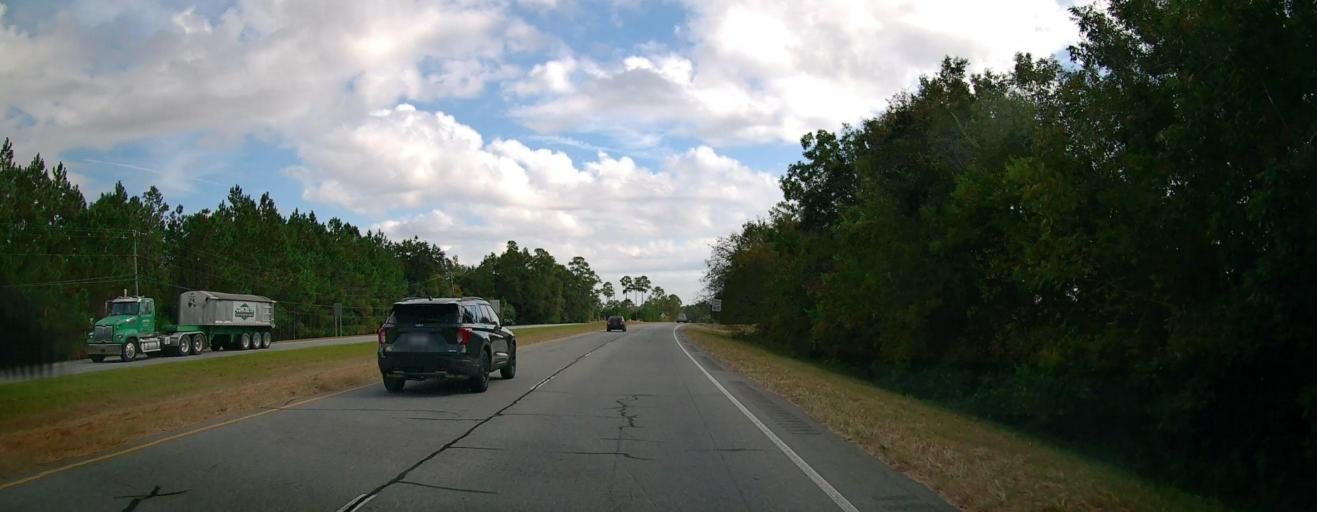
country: US
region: Georgia
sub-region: Mitchell County
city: Camilla
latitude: 31.2153
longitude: -84.1823
